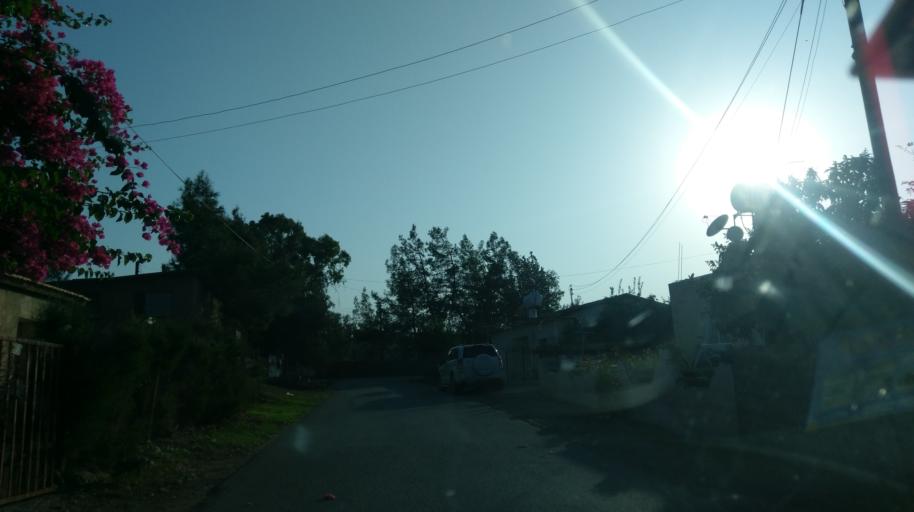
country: CY
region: Lefkosia
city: Lefka
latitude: 35.1286
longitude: 32.9117
